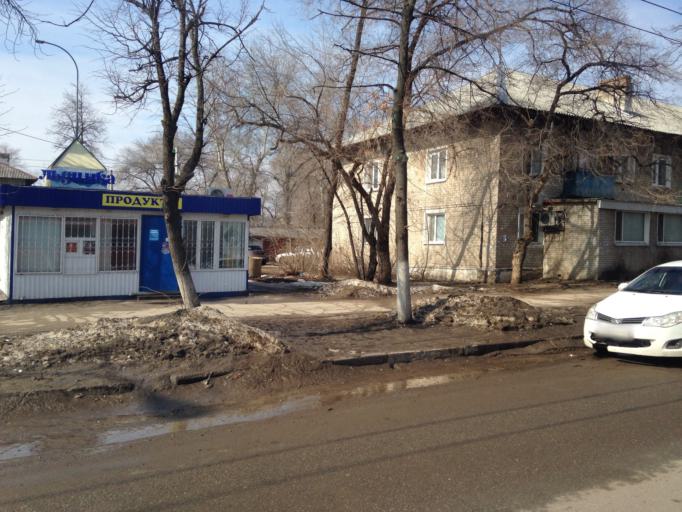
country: RU
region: Ulyanovsk
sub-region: Ulyanovskiy Rayon
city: Ulyanovsk
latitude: 54.3472
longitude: 48.5485
